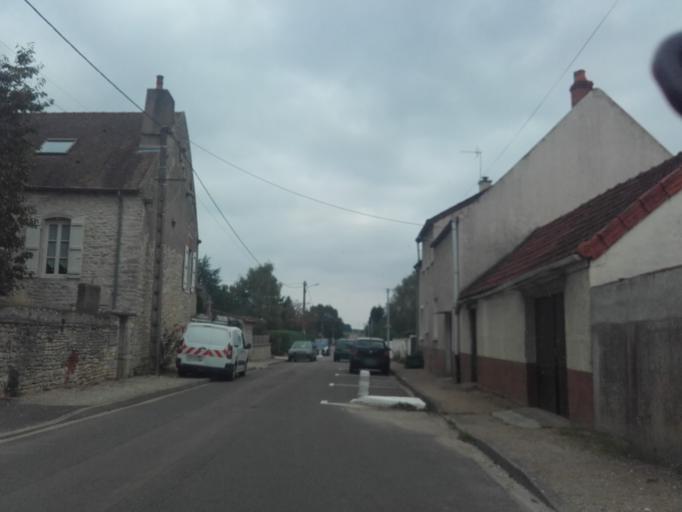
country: FR
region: Bourgogne
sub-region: Departement de Saone-et-Loire
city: Chagny
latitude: 46.8988
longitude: 4.7685
